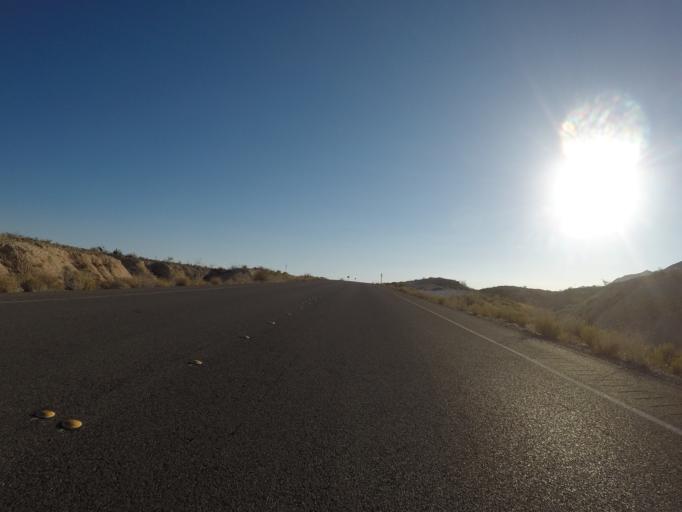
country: US
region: Nevada
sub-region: Clark County
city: Moapa Valley
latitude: 36.3955
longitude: -114.4247
